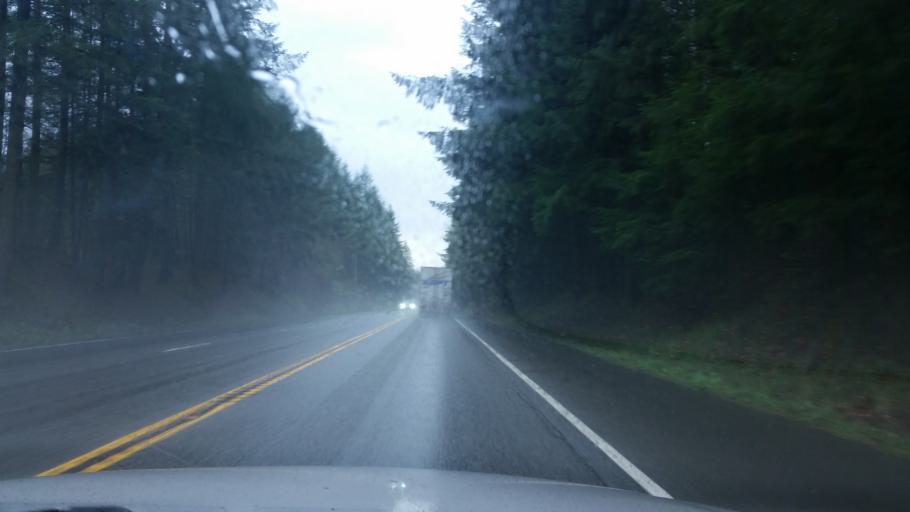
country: US
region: Washington
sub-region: King County
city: Hobart
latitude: 47.4455
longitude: -121.9612
